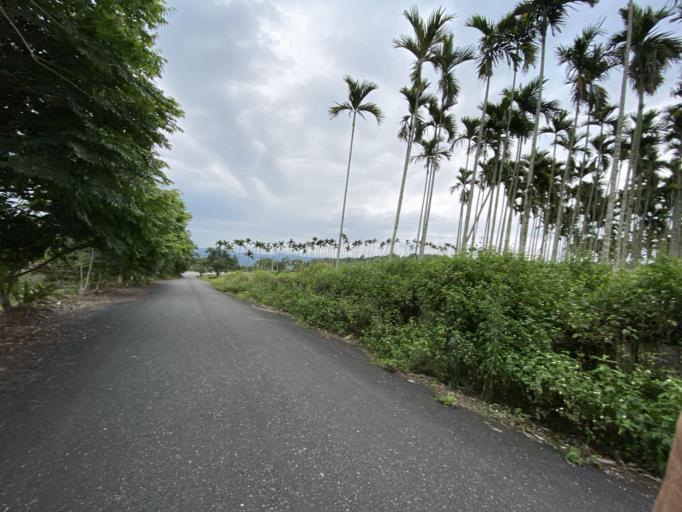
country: TW
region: Taiwan
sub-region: Hualien
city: Hualian
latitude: 23.4718
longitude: 121.3593
